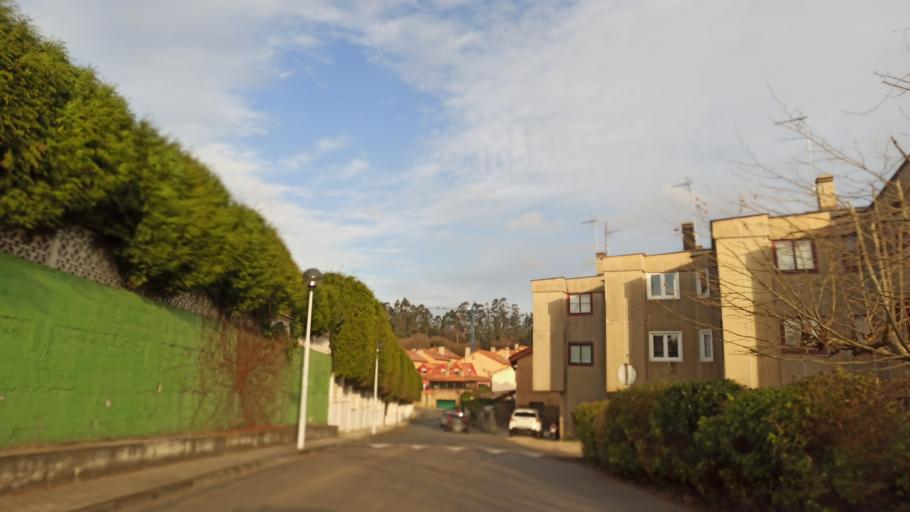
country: ES
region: Galicia
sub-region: Provincia da Coruna
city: Cambre
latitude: 43.3241
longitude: -8.3500
